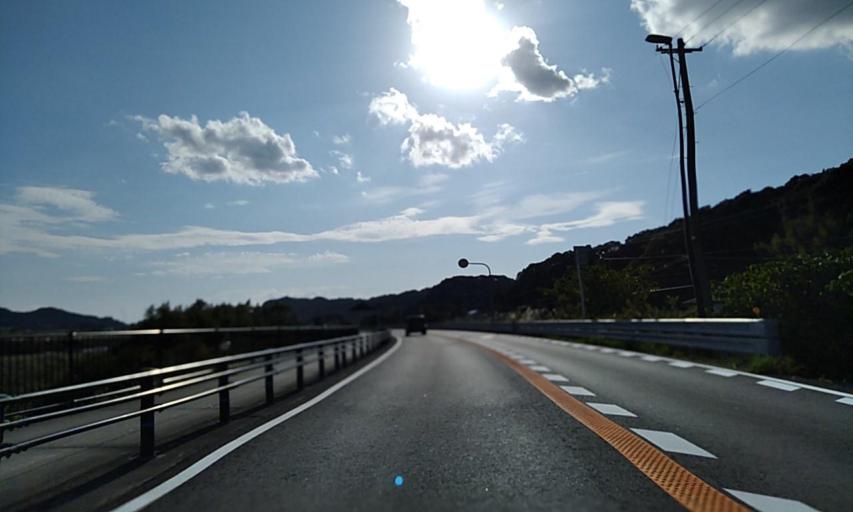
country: JP
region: Wakayama
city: Tanabe
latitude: 33.6855
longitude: 135.4129
